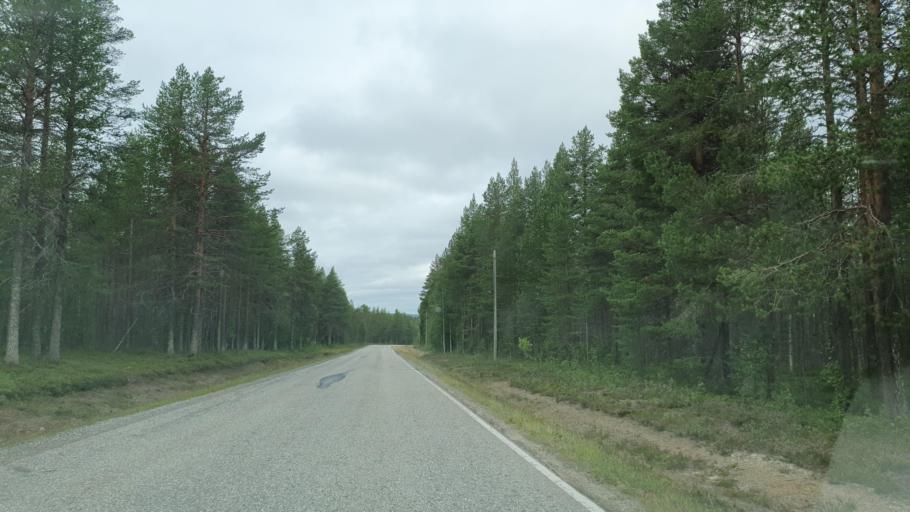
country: FI
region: Lapland
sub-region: Pohjois-Lappi
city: Sodankylae
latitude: 67.4162
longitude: 26.2586
